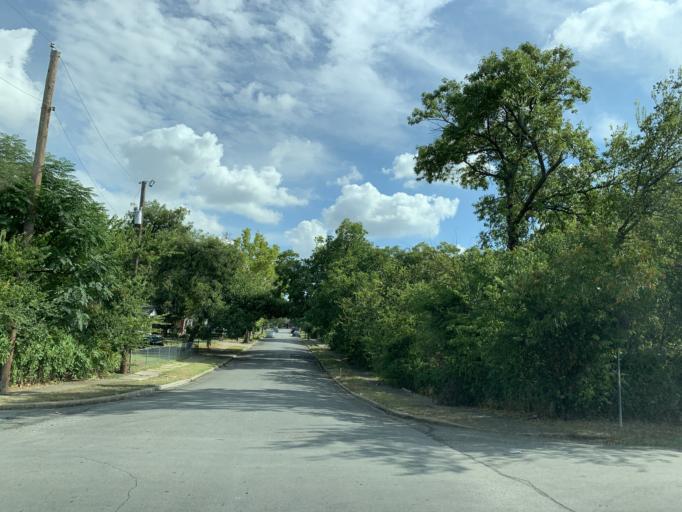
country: US
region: Texas
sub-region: Dallas County
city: Cockrell Hill
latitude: 32.7375
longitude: -96.8480
